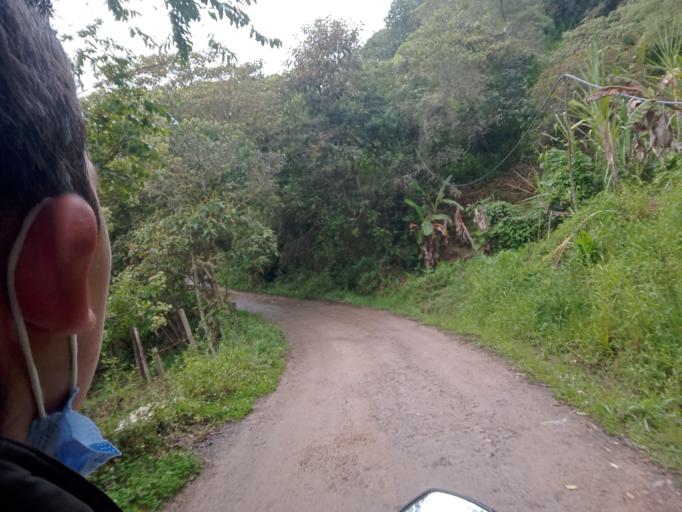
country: CO
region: Cundinamarca
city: Tenza
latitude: 5.1026
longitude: -73.4214
